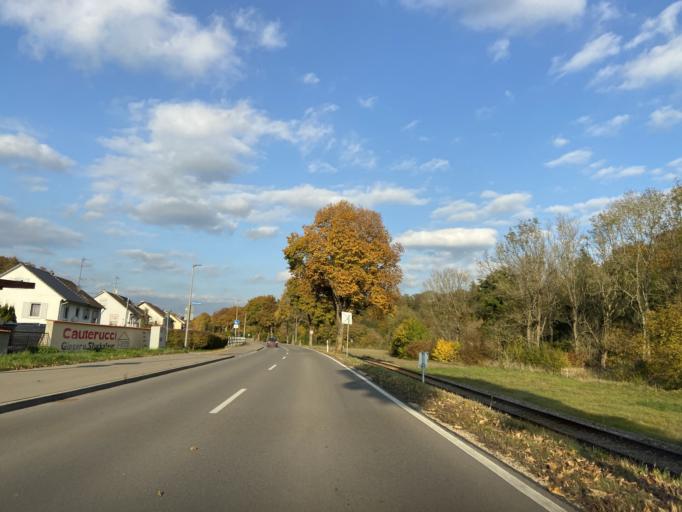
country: DE
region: Baden-Wuerttemberg
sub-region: Tuebingen Region
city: Sigmaringendorf
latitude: 48.0761
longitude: 9.2705
